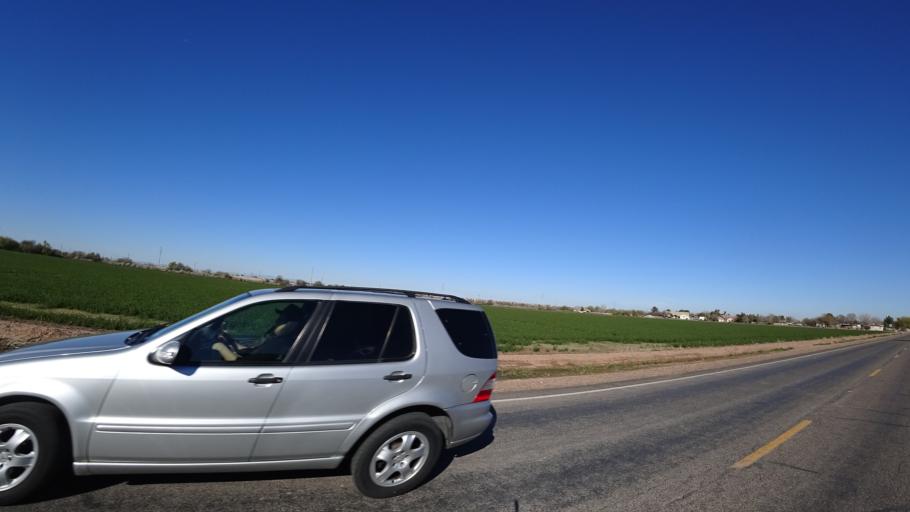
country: US
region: Arizona
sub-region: Maricopa County
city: Tolleson
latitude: 33.3921
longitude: -112.2825
